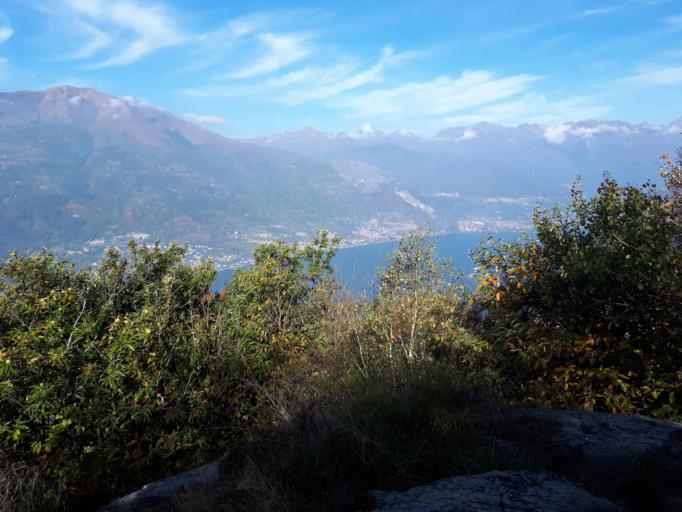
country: IT
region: Lombardy
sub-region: Provincia di Lecco
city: Vestreno
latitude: 46.0682
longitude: 9.3231
